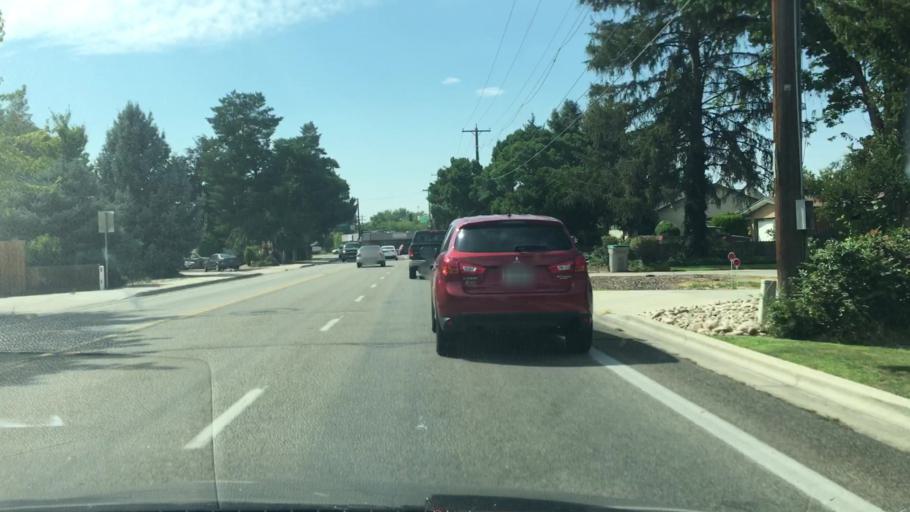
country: US
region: Idaho
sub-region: Ada County
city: Garden City
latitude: 43.6433
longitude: -116.2762
